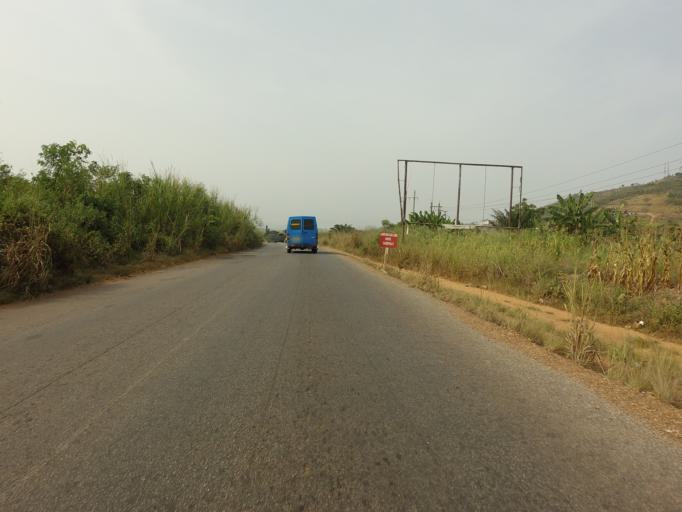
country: GH
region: Volta
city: Ho
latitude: 6.6072
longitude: 0.4542
